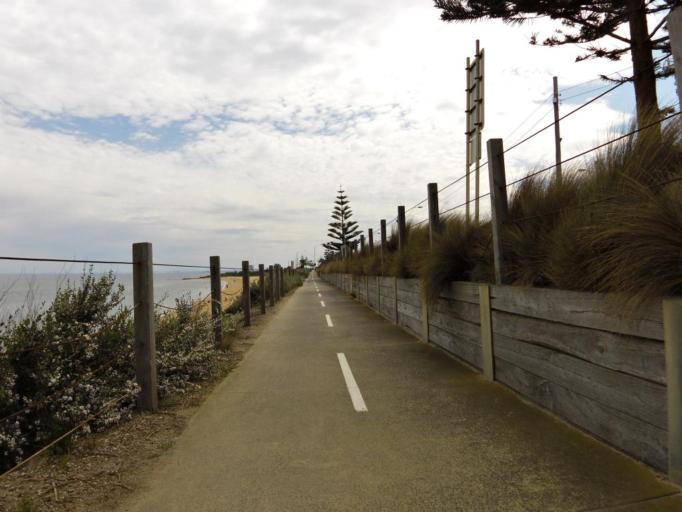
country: AU
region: Victoria
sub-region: Bayside
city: Hampton
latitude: -37.9291
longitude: 144.9901
